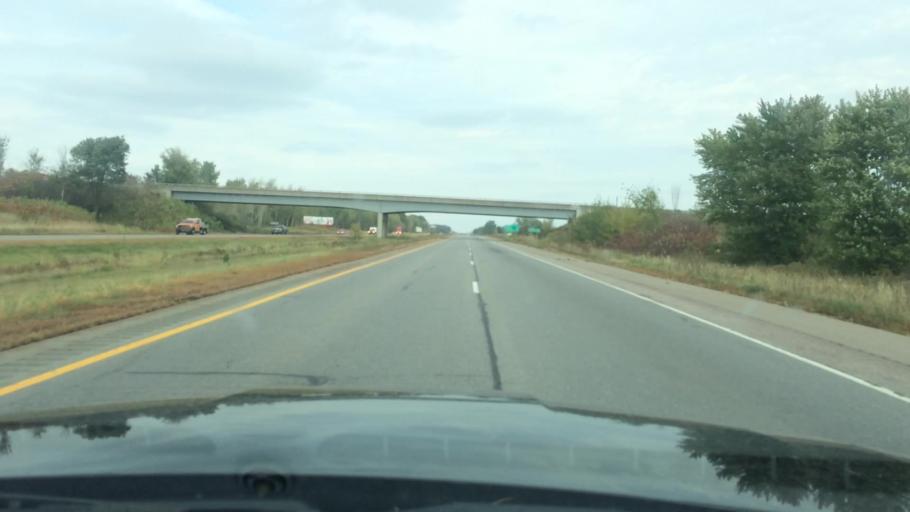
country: US
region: Wisconsin
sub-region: Marathon County
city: Mosinee
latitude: 44.7414
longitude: -89.6796
